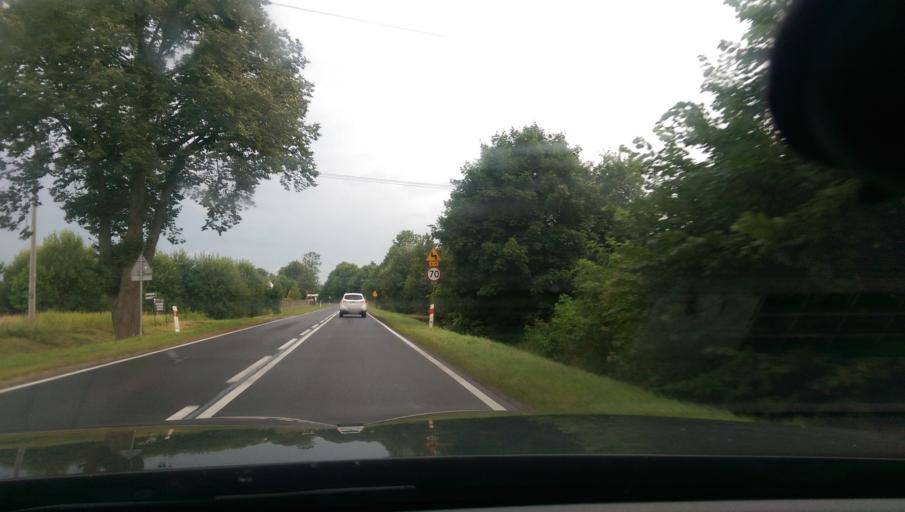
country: PL
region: Warmian-Masurian Voivodeship
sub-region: Powiat szczycienski
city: Szczytno
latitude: 53.5480
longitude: 20.9887
